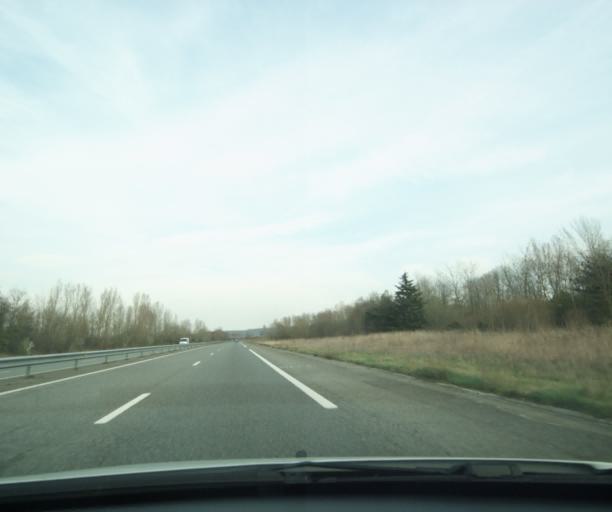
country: FR
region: Midi-Pyrenees
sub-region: Departement des Hautes-Pyrenees
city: Laloubere
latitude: 43.2133
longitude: 0.0780
